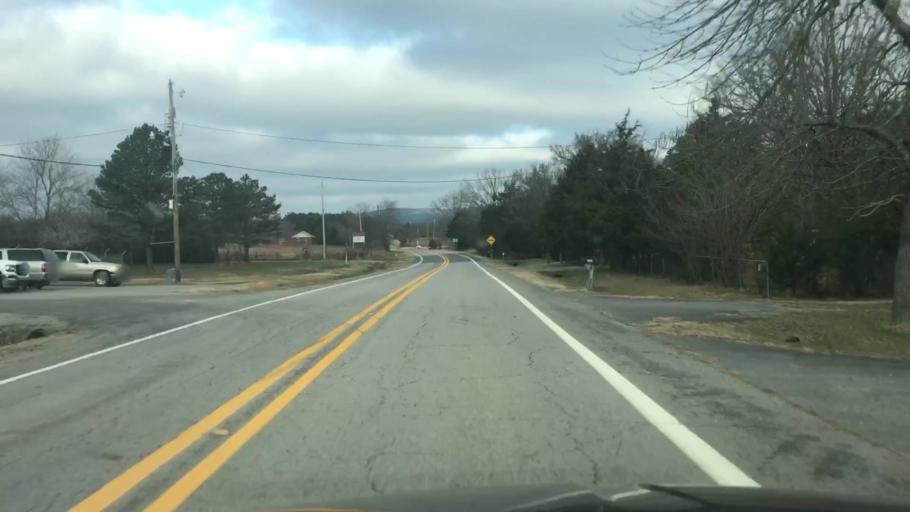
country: US
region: Arkansas
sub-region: Montgomery County
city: Mount Ida
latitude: 34.6318
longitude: -93.7354
